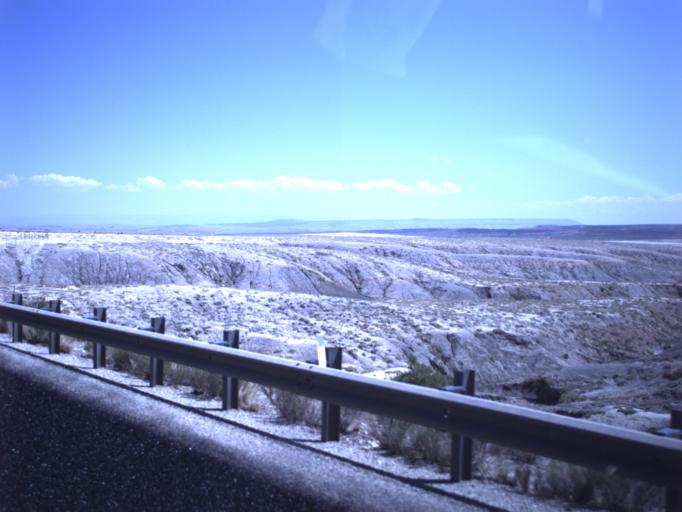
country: US
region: Utah
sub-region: Emery County
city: Ferron
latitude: 39.0346
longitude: -111.1287
